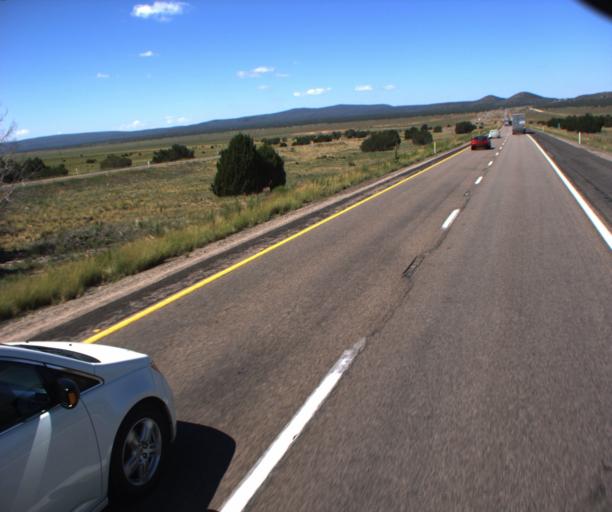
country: US
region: Arizona
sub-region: Mohave County
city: Peach Springs
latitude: 35.3164
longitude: -112.9628
